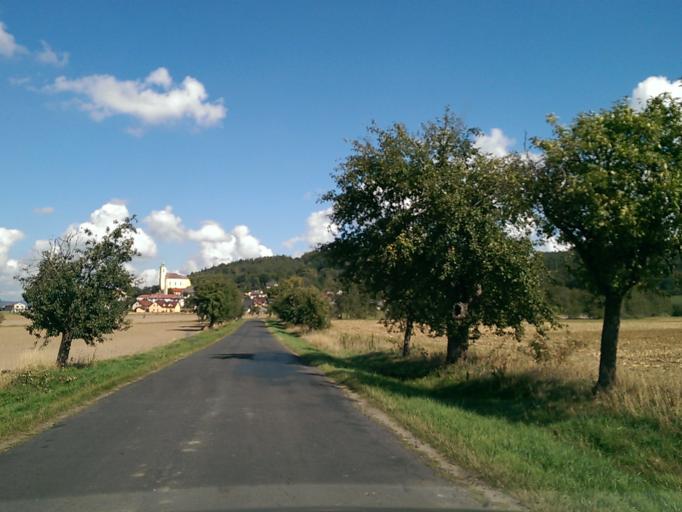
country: CZ
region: Central Bohemia
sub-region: Okres Mlada Boleslav
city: Zd'ar
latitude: 50.5543
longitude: 15.0984
